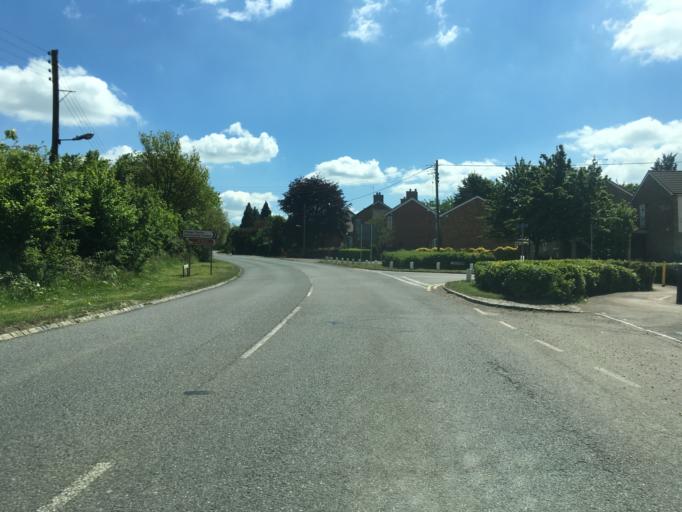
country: GB
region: England
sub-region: Milton Keynes
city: Wavendon
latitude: 52.0272
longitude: -0.6684
